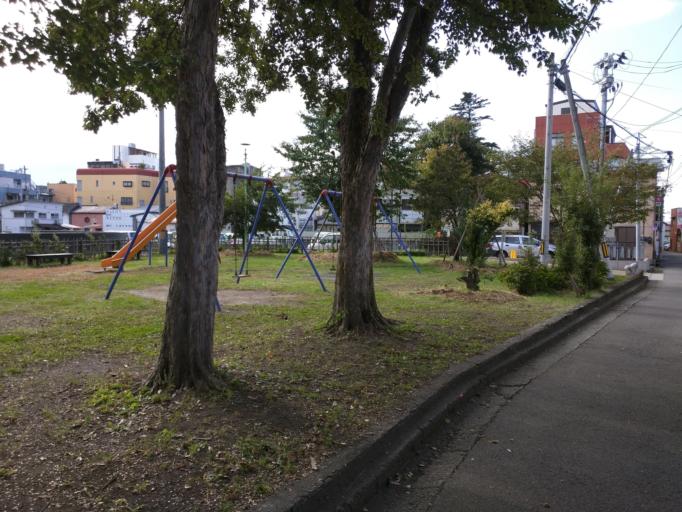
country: JP
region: Fukushima
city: Kitakata
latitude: 37.4972
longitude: 139.9299
